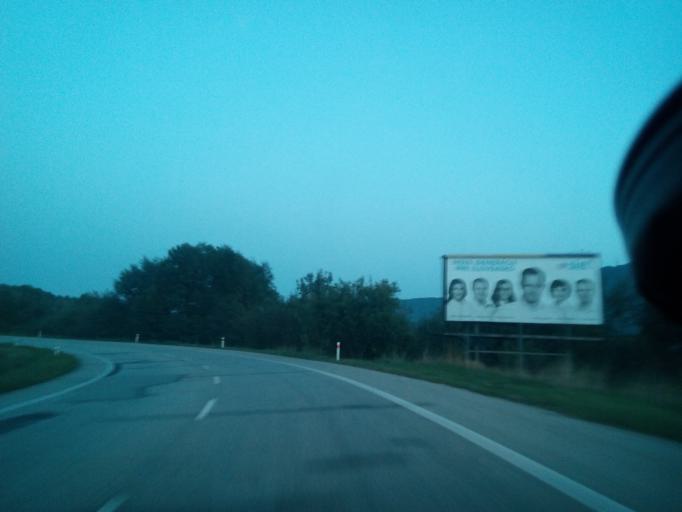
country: SK
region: Kosicky
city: Roznava
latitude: 48.6404
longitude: 20.5253
